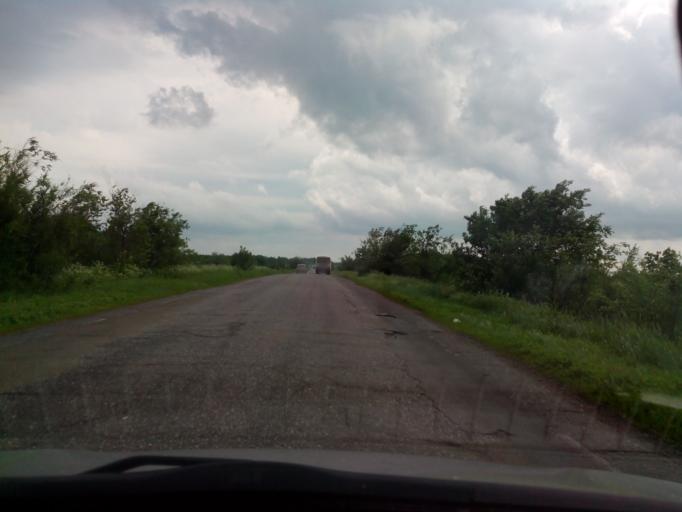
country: RU
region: Volgograd
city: Mikhaylovka
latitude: 49.9641
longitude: 43.0320
